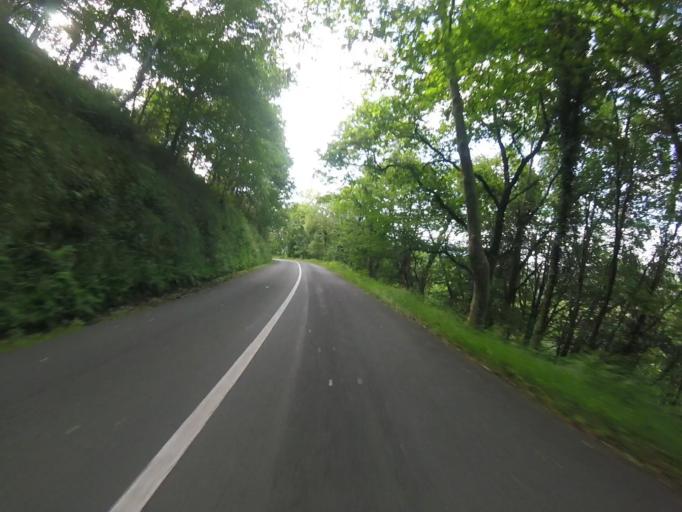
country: ES
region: Basque Country
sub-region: Provincia de Guipuzcoa
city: Errenteria
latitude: 43.2757
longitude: -1.8494
